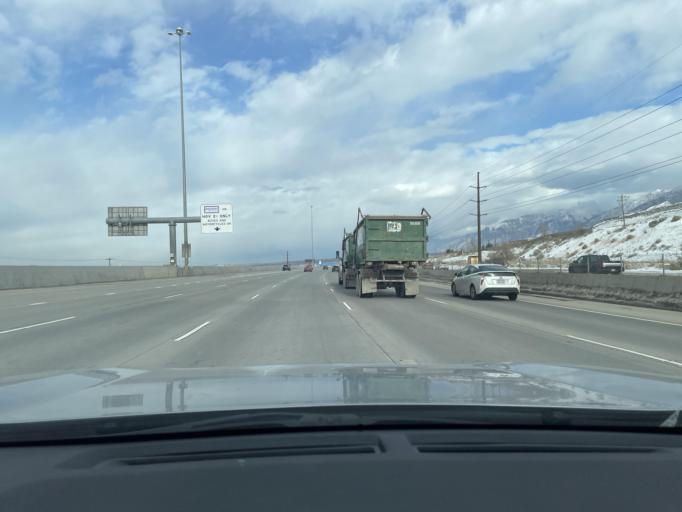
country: US
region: Utah
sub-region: Salt Lake County
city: Draper
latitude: 40.4861
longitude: -111.8897
